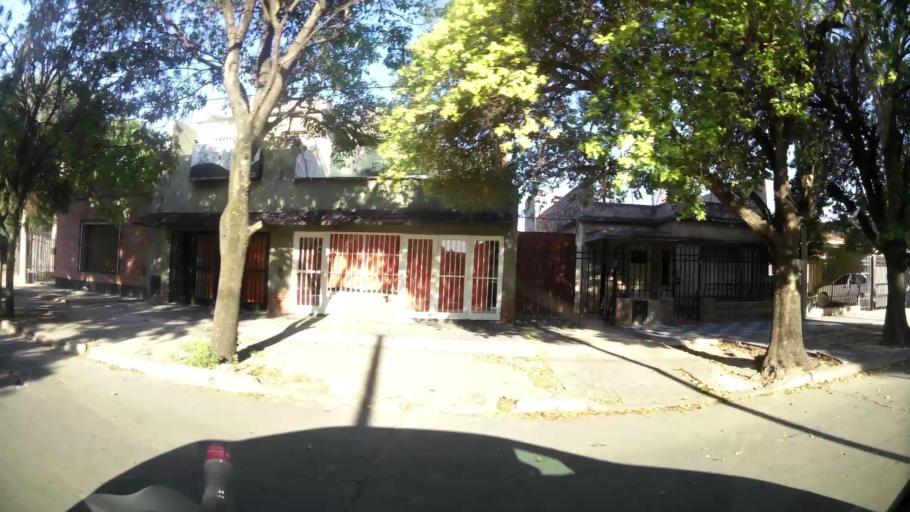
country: AR
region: Cordoba
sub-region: Departamento de Capital
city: Cordoba
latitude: -31.3785
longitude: -64.1825
